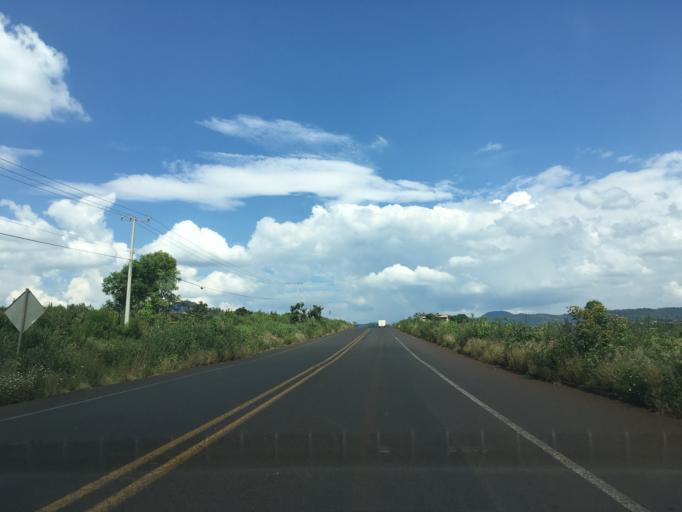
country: MX
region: Michoacan
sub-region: Tingueindin
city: Tingueindin
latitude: 19.8387
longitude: -102.4904
